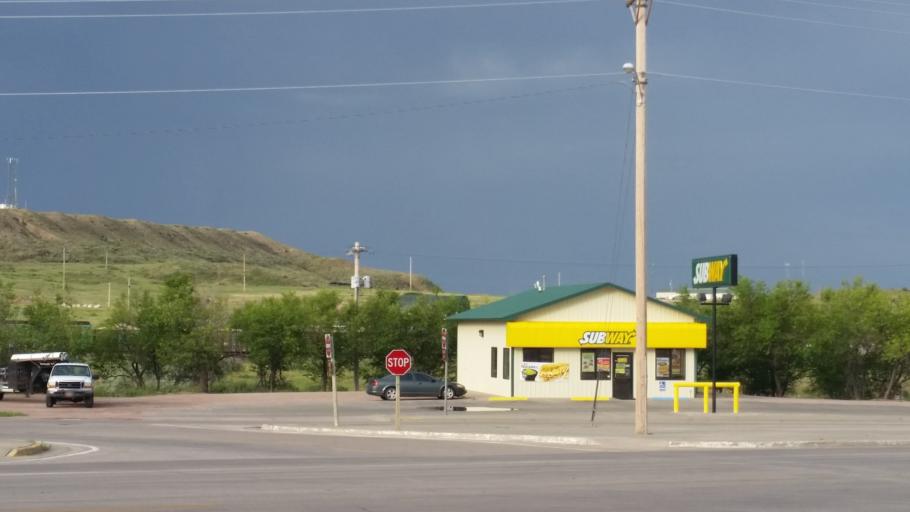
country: US
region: Wyoming
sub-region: Weston County
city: Newcastle
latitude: 43.8489
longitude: -104.1947
